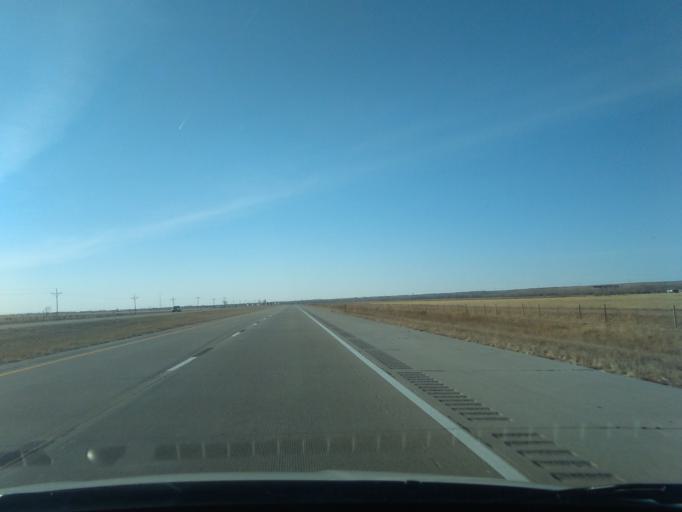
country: US
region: Colorado
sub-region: Sedgwick County
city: Julesburg
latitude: 41.0626
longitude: -102.0003
